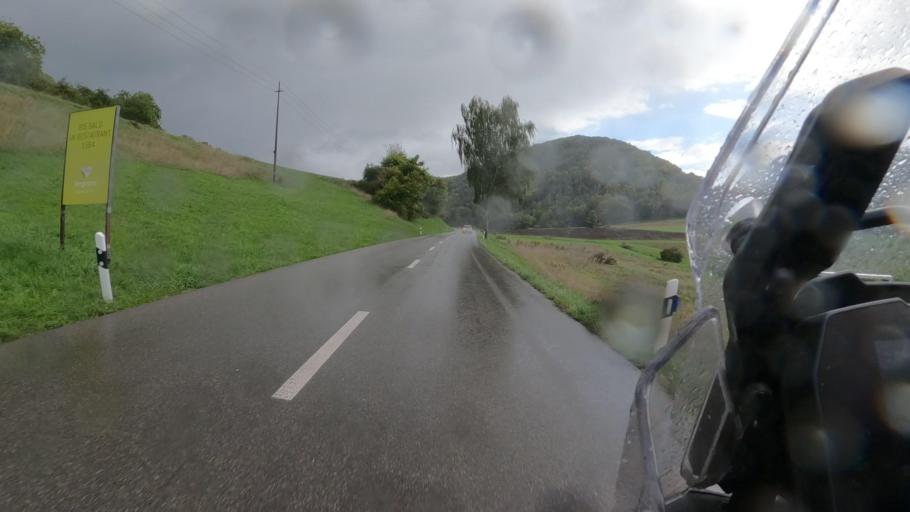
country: CH
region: Schaffhausen
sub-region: Bezirk Unterklettgau
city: Wilchingen
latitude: 47.6546
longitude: 8.4855
